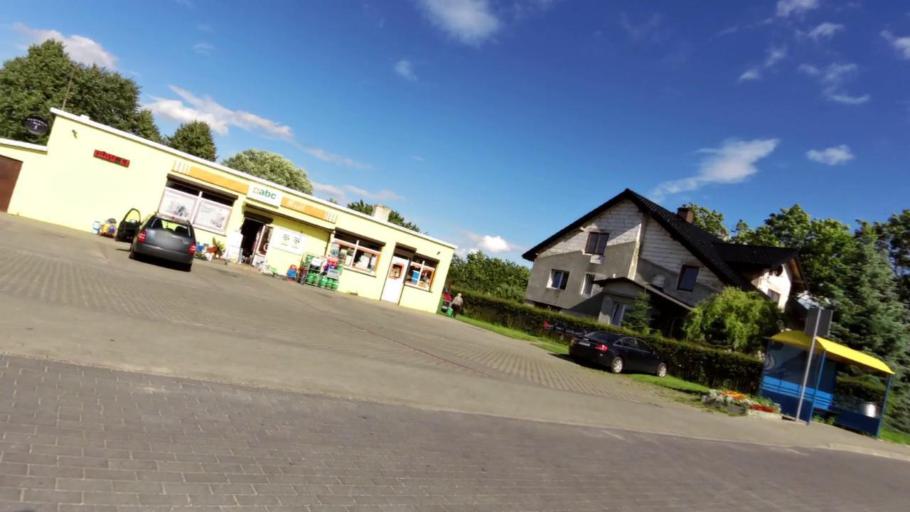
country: PL
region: West Pomeranian Voivodeship
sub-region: Powiat slawienski
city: Slawno
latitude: 54.4344
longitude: 16.7352
